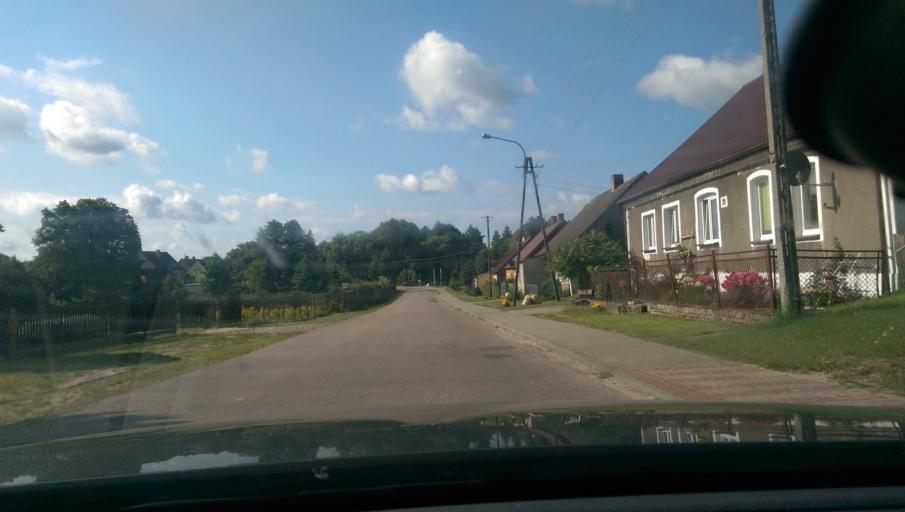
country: PL
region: West Pomeranian Voivodeship
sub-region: Powiat walecki
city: Walcz
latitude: 53.3472
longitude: 16.5700
